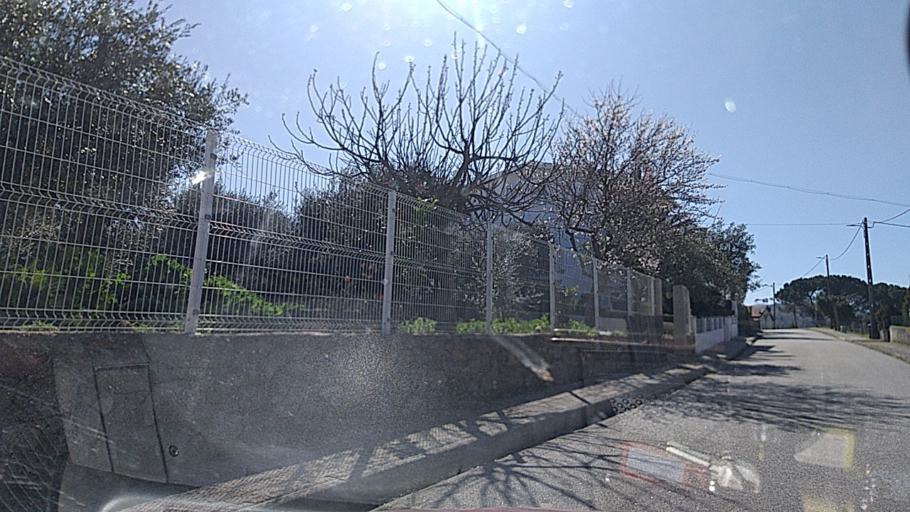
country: PT
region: Guarda
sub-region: Celorico da Beira
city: Celorico da Beira
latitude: 40.6181
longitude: -7.4069
